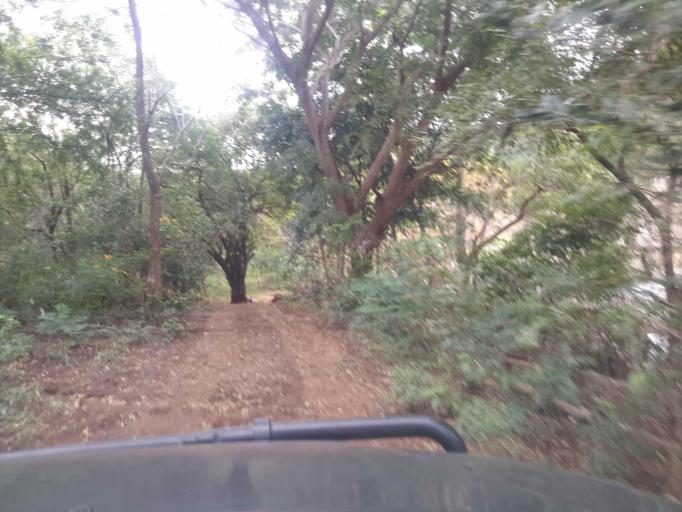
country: NI
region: Carazo
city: Santa Teresa
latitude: 11.6883
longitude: -86.2980
